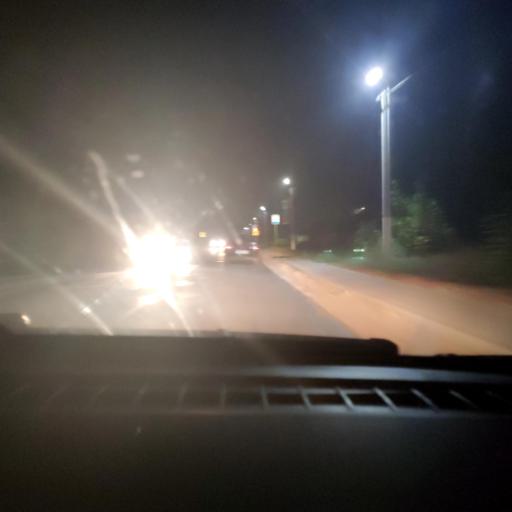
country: RU
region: Voronezj
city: Novaya Usman'
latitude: 51.6430
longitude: 39.3313
